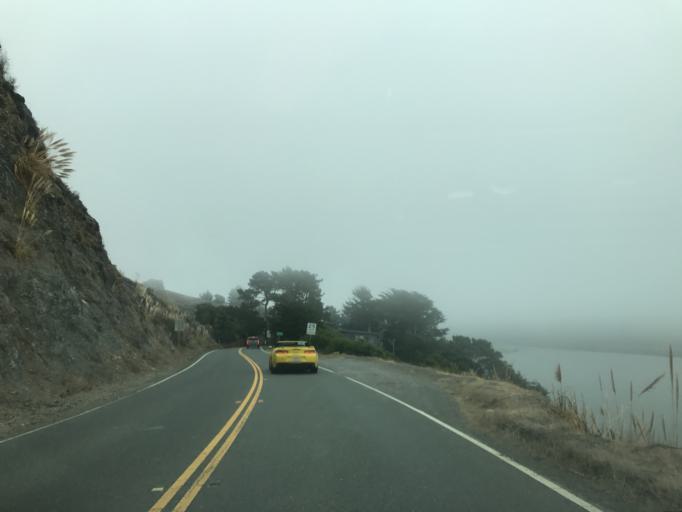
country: US
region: California
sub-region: Sonoma County
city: Monte Rio
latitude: 38.4521
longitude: -123.1277
